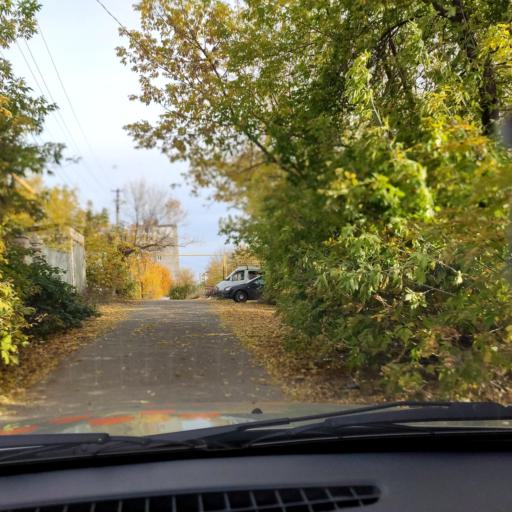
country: RU
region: Bashkortostan
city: Ufa
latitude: 54.7013
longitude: 55.9829
